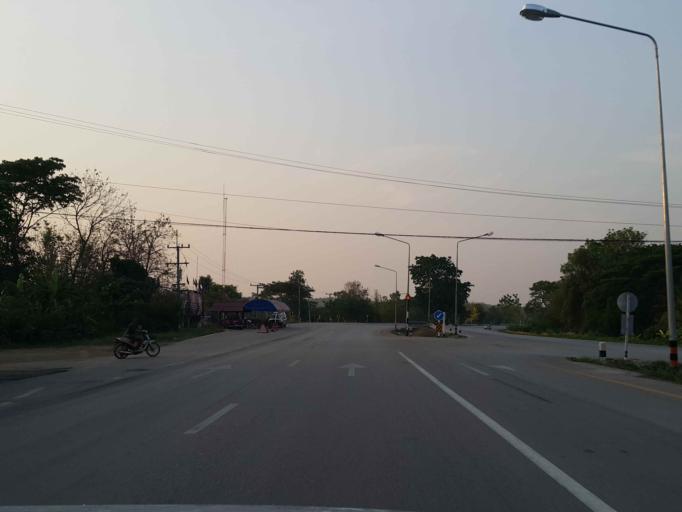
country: TH
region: Lampang
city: Sop Prap
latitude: 17.9503
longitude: 99.3509
